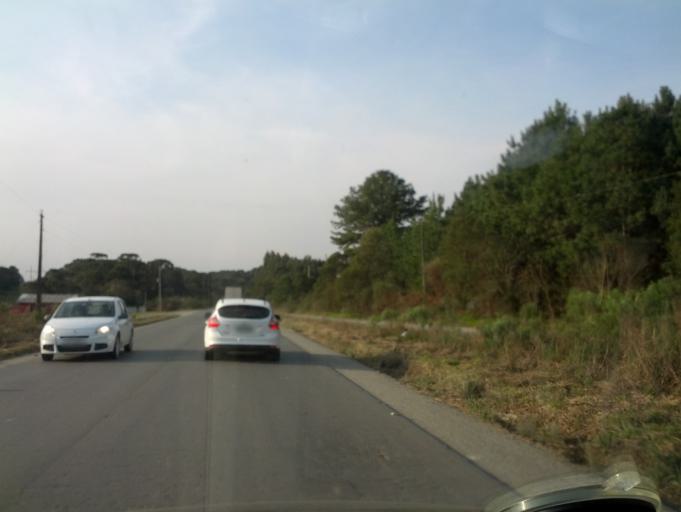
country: BR
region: Santa Catarina
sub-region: Otacilio Costa
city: Otacilio Costa
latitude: -27.5373
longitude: -50.1437
